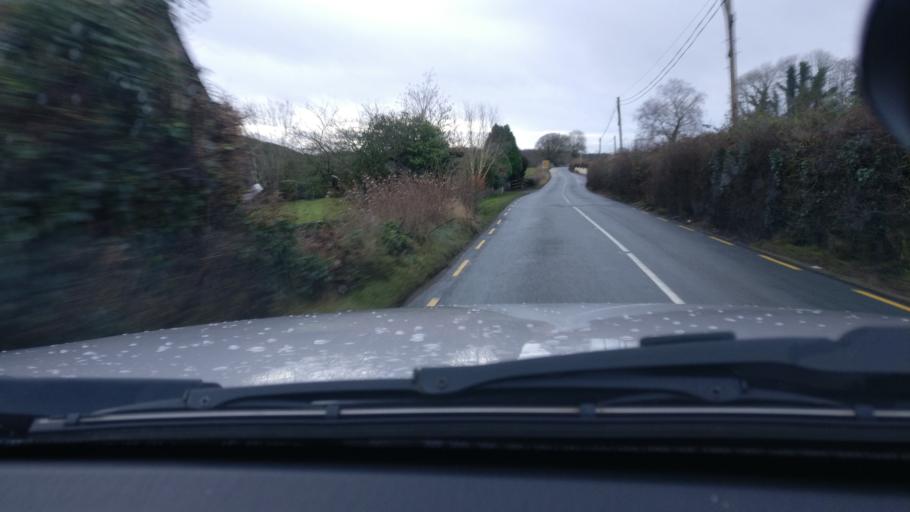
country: IE
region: Leinster
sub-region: An Longfort
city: Granard
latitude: 53.7992
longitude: -7.3897
